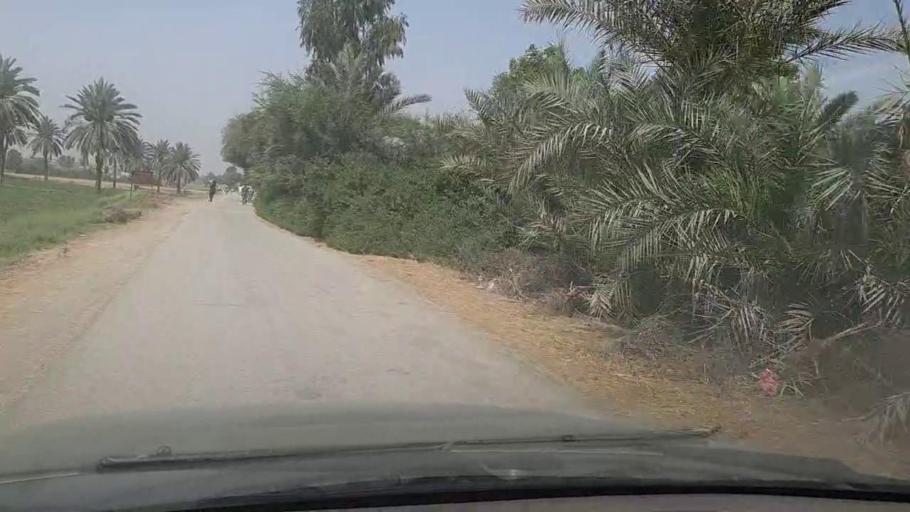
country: PK
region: Sindh
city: Madeji
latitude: 27.7984
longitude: 68.4129
